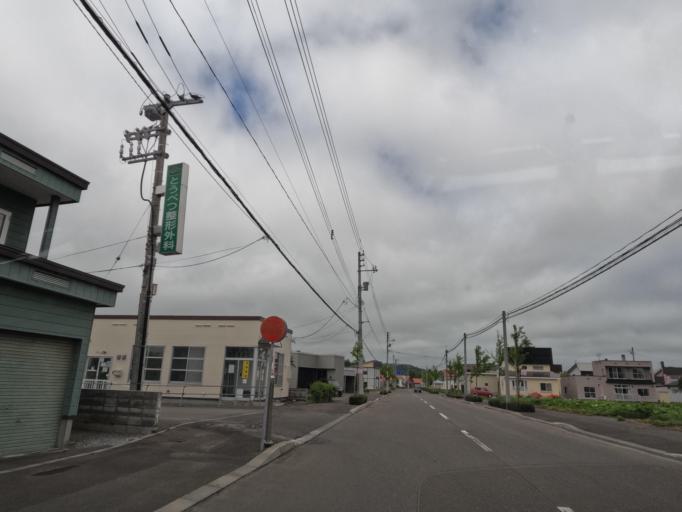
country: JP
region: Hokkaido
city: Tobetsu
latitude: 43.2357
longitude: 141.5141
